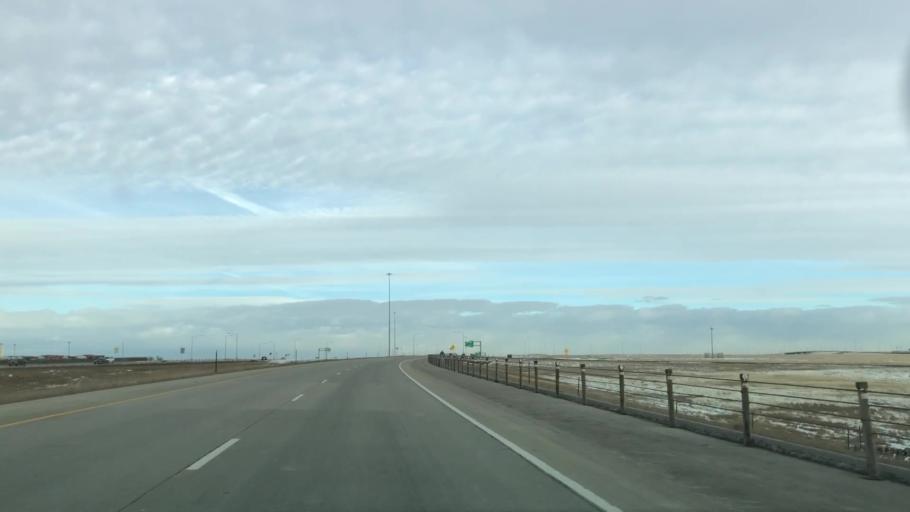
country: US
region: Colorado
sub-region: Adams County
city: Aurora
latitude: 39.8338
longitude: -104.7692
